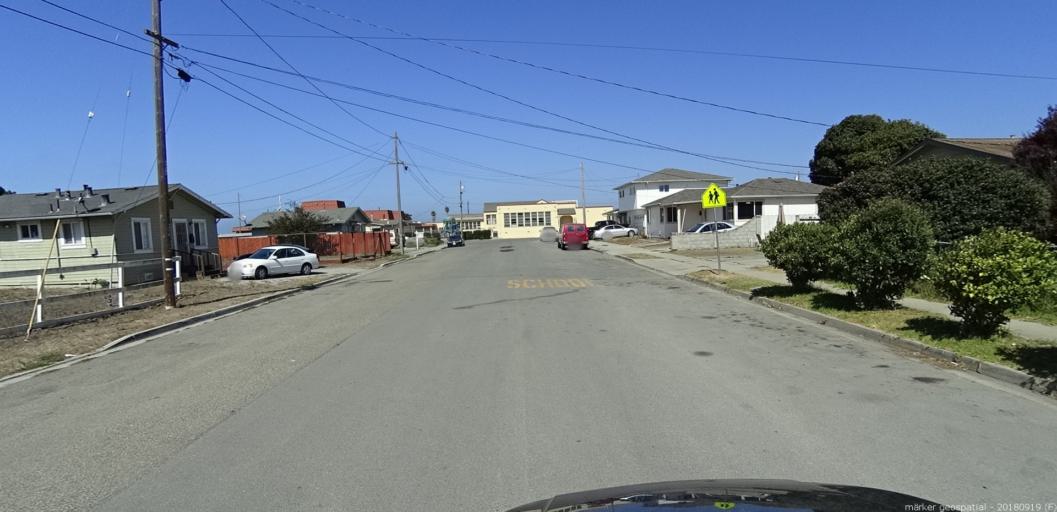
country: US
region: California
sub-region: Monterey County
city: Castroville
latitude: 36.7628
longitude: -121.7522
